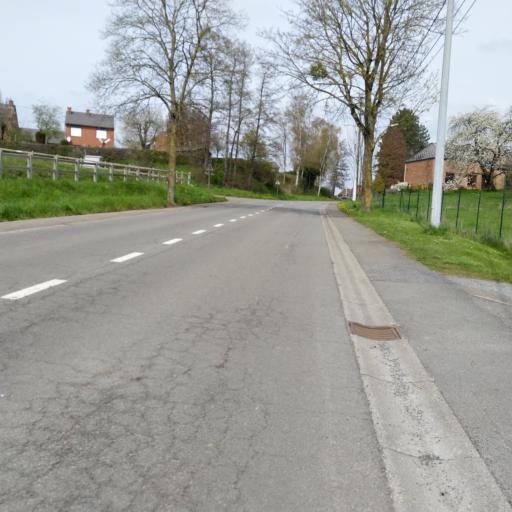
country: BE
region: Wallonia
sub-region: Province du Hainaut
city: Quevy-le-Petit
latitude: 50.3725
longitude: 3.9249
